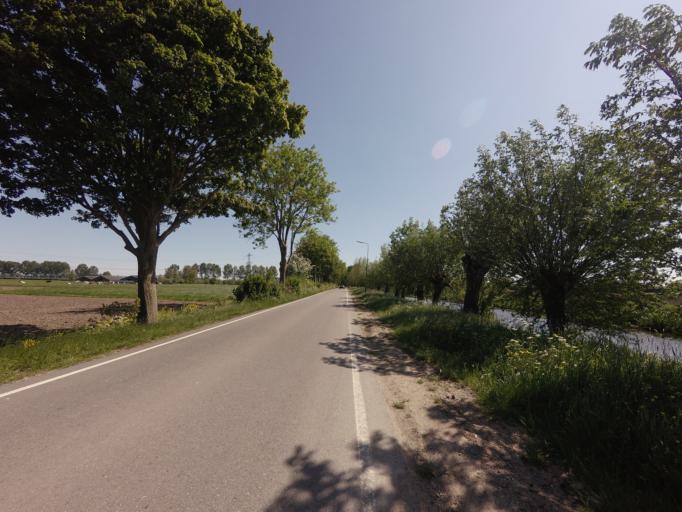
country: NL
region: Utrecht
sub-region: Gemeente Woerden
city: Woerden
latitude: 52.1081
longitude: 4.9387
